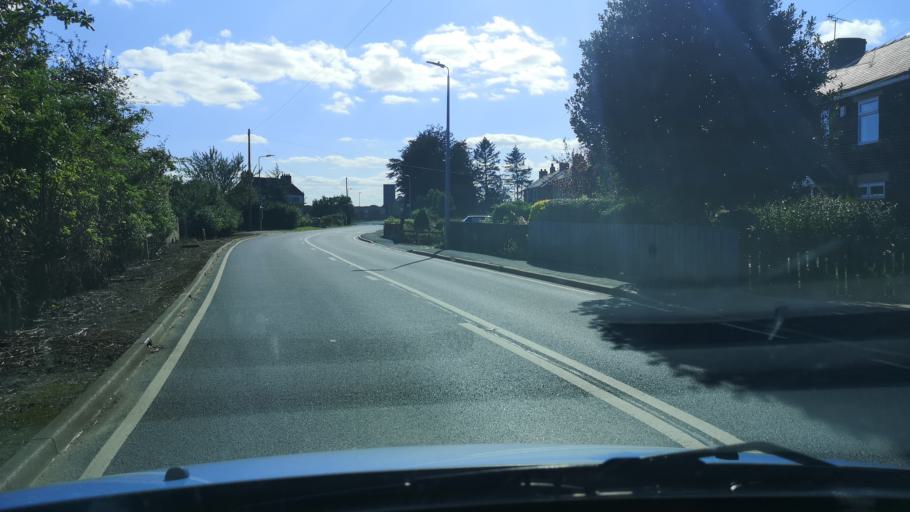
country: GB
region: England
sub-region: North Lincolnshire
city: Eastoft
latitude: 53.6342
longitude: -0.7893
